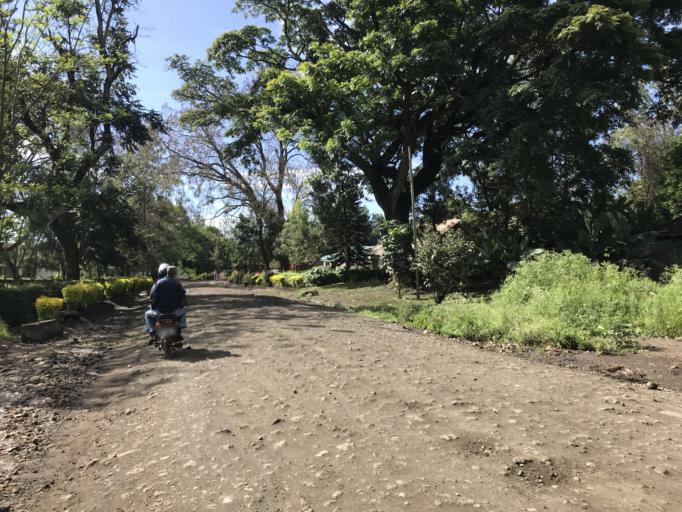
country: TZ
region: Arusha
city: Nkoaranga
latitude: -3.3838
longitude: 36.7957
